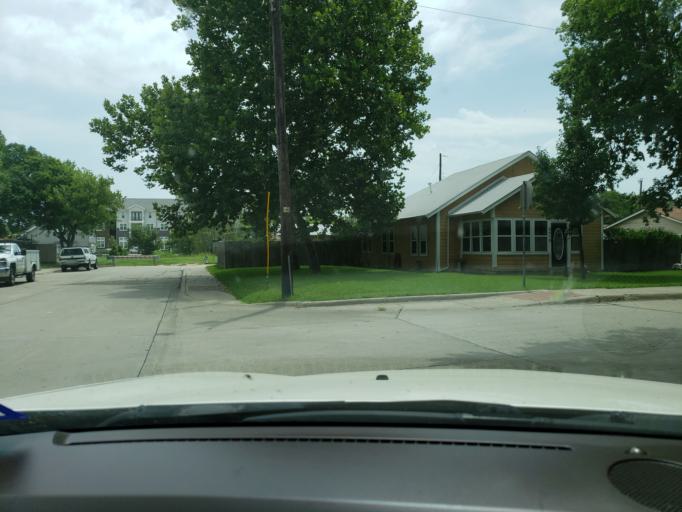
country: US
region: Texas
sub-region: Dallas County
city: Rowlett
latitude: 32.9010
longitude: -96.5667
